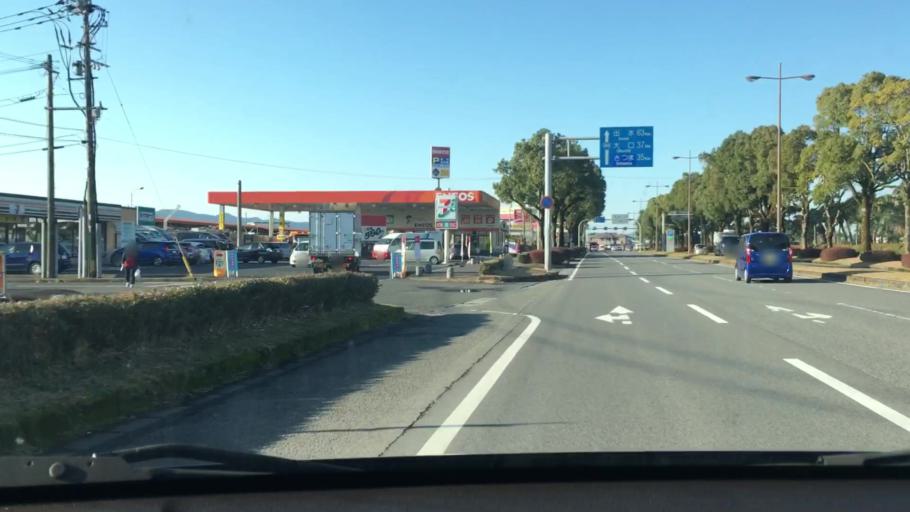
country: JP
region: Kagoshima
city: Kajiki
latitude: 31.7997
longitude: 130.7152
